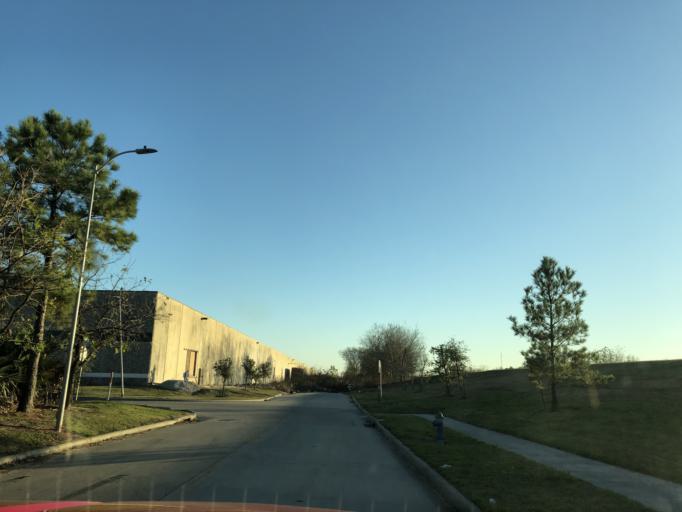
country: US
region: Texas
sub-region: Harris County
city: Jacinto City
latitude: 29.7588
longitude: -95.2687
